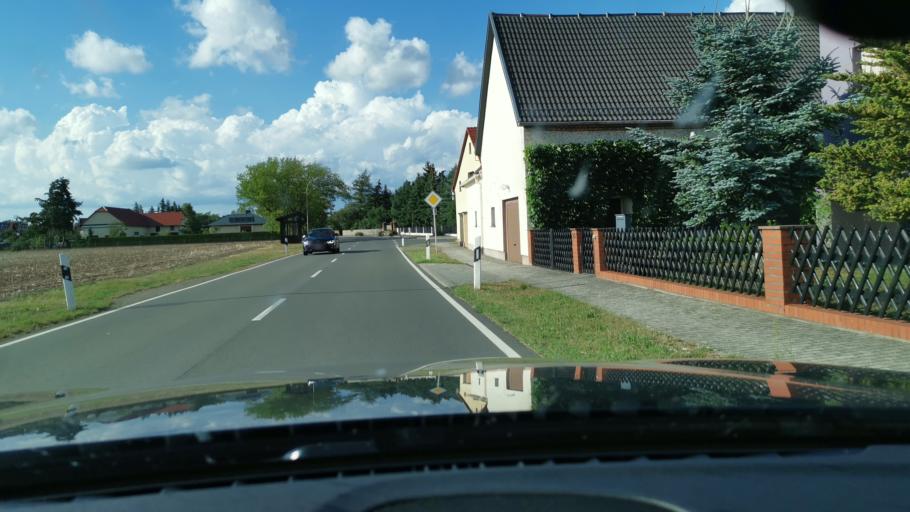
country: DE
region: Saxony
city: Bad Duben
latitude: 51.5580
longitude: 12.5729
